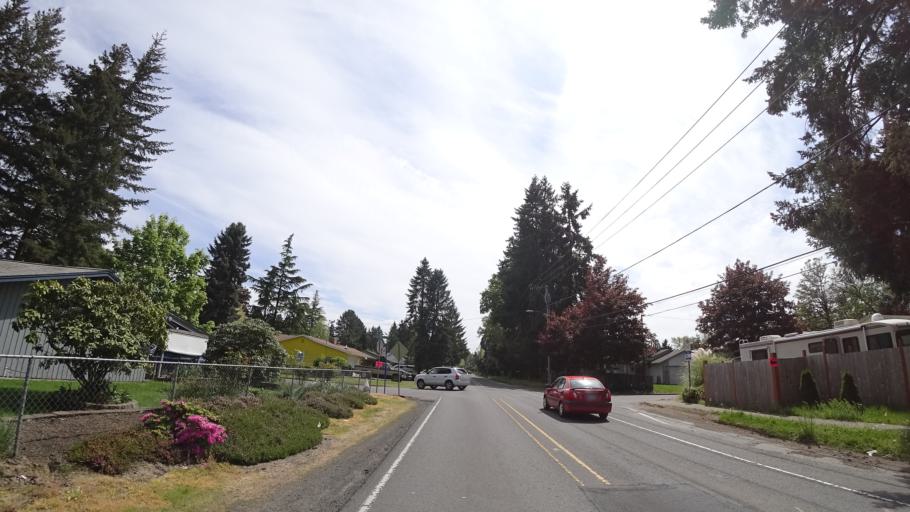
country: US
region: Oregon
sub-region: Washington County
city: Aloha
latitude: 45.4822
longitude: -122.8815
